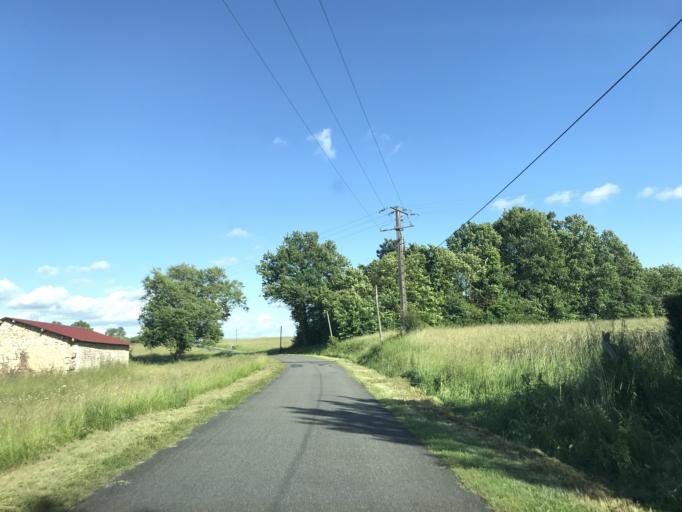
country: FR
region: Poitou-Charentes
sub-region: Departement de la Charente
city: Chalais
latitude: 45.2744
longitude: -0.0261
